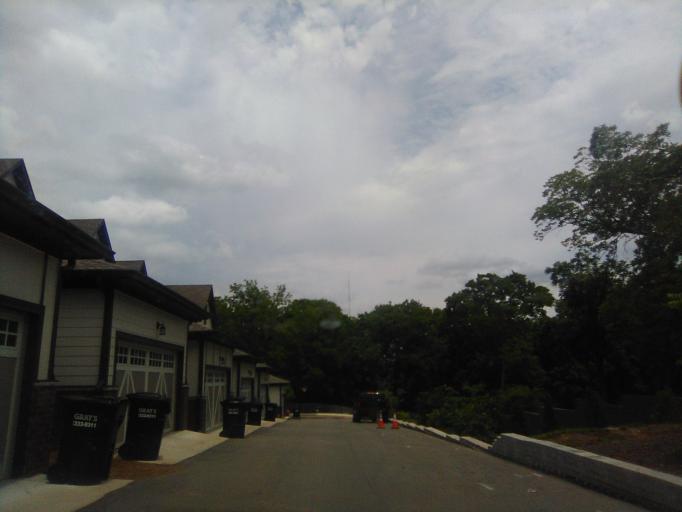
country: US
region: Tennessee
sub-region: Davidson County
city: Belle Meade
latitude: 36.1329
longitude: -86.8894
